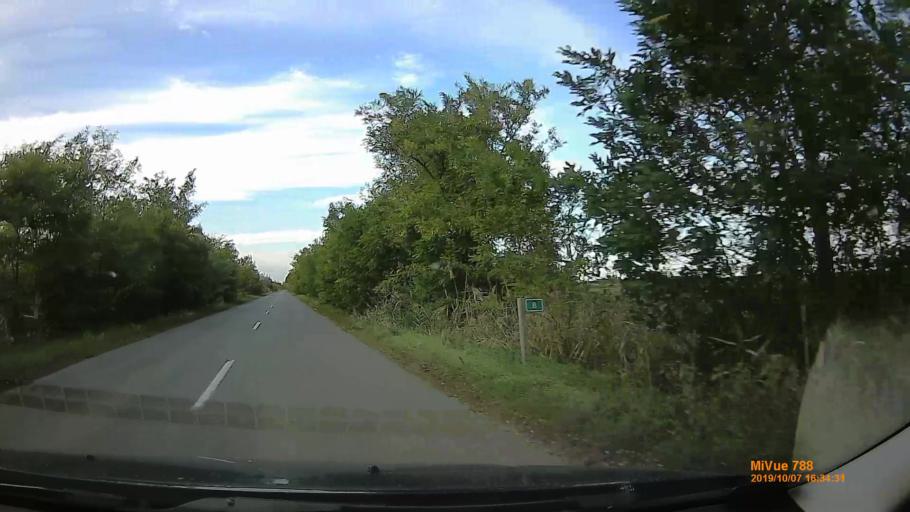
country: HU
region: Bekes
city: Szarvas
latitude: 46.8020
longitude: 20.6201
